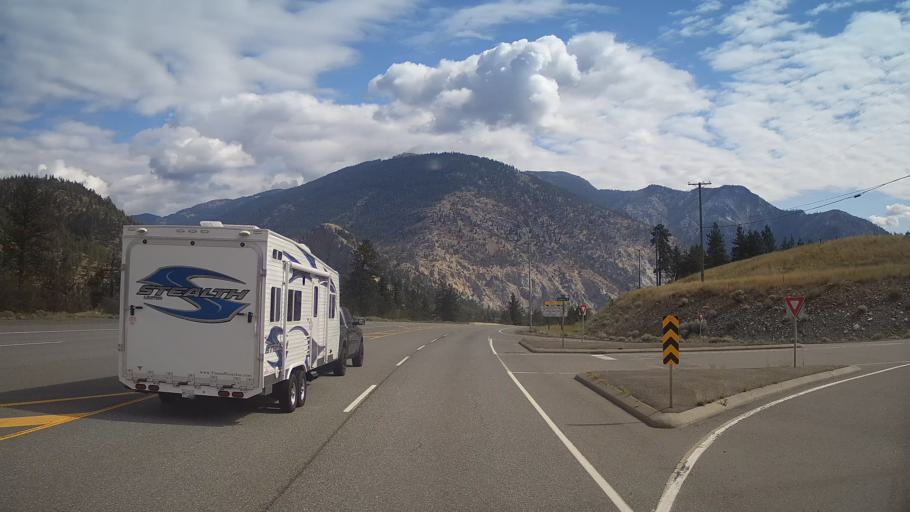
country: CA
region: British Columbia
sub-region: Thompson-Nicola Regional District
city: Ashcroft
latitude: 50.2463
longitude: -121.5692
